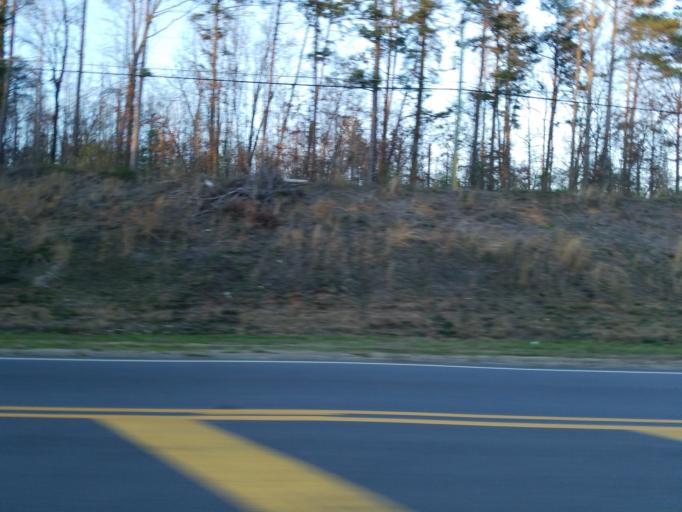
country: US
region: Georgia
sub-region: Hall County
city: Oakwood
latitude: 34.3116
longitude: -83.9935
